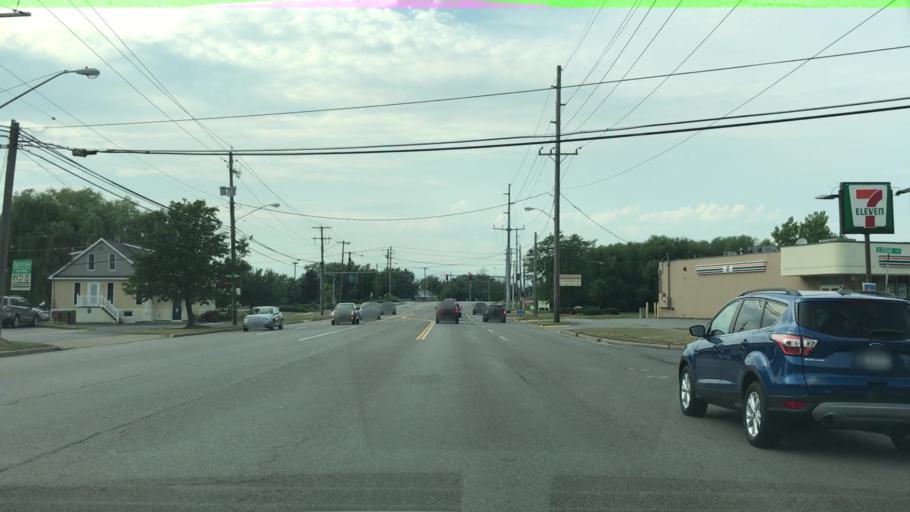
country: US
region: New York
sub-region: Erie County
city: Cheektowaga
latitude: 42.9227
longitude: -78.7405
